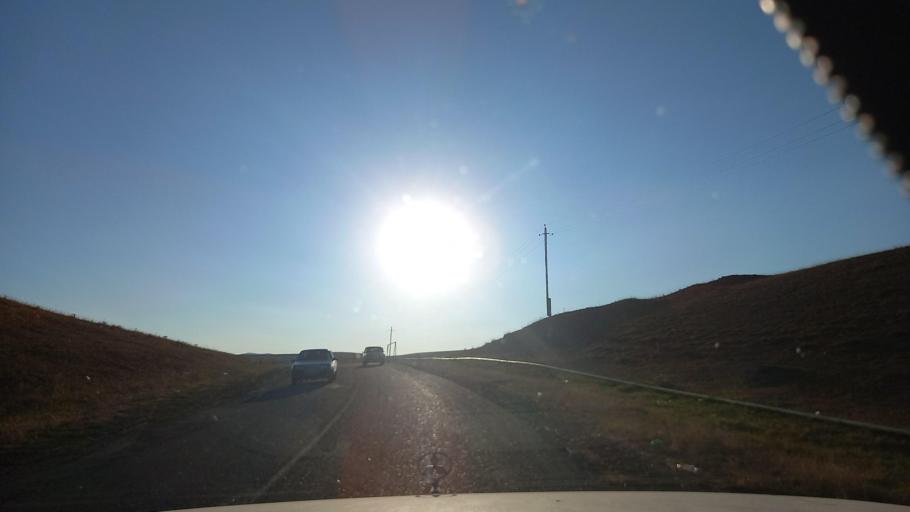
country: AZ
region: Shamkir Rayon
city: Shamkhor
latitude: 40.7638
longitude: 45.9250
